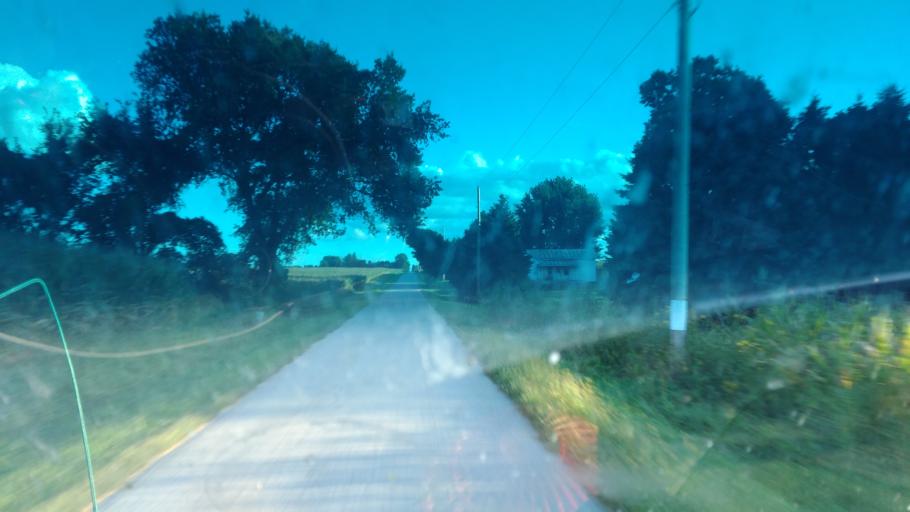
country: US
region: Ohio
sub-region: Wyandot County
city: Upper Sandusky
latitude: 40.8700
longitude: -83.1508
